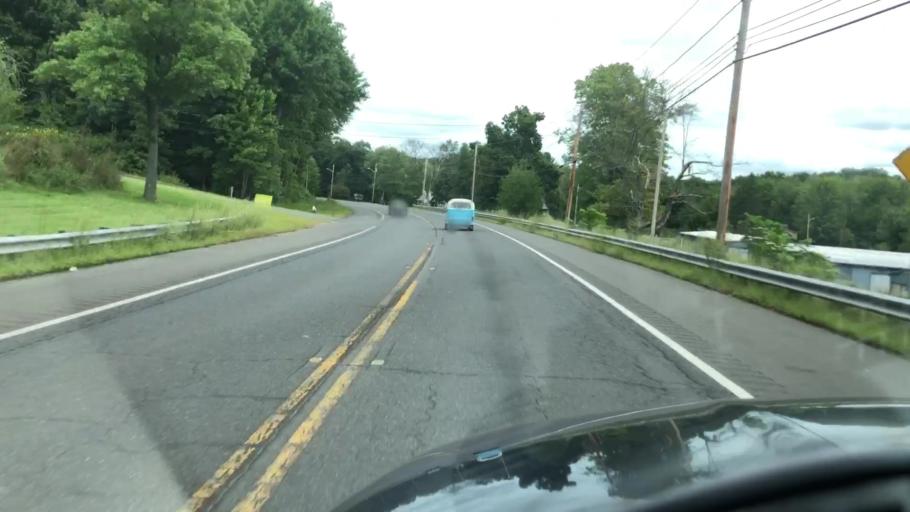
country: US
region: Massachusetts
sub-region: Hampshire County
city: Easthampton
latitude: 42.2908
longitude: -72.6592
